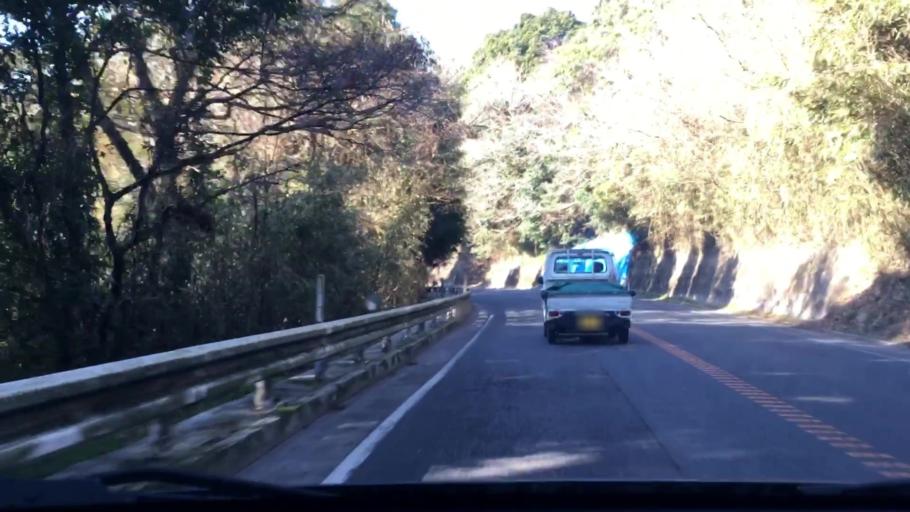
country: JP
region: Kagoshima
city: Sueyoshicho-ninokata
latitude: 31.6658
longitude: 130.9083
